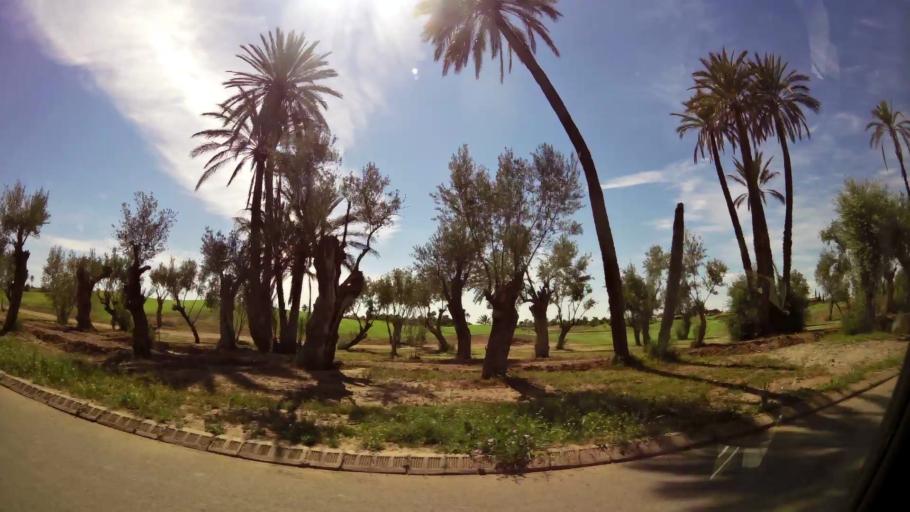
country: MA
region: Marrakech-Tensift-Al Haouz
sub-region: Marrakech
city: Marrakesh
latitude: 31.6179
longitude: -7.9366
